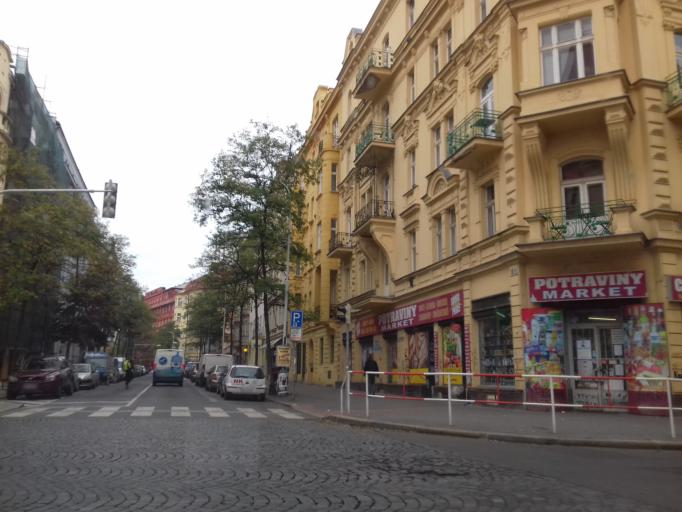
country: CZ
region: Praha
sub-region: Praha 8
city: Karlin
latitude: 50.0789
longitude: 14.4483
